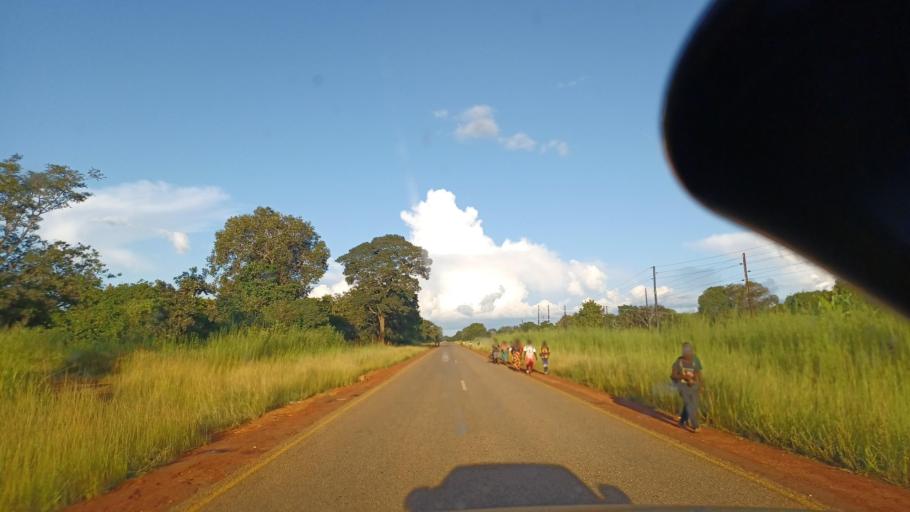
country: ZM
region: North-Western
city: Kalengwa
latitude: -13.1439
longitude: 25.0457
